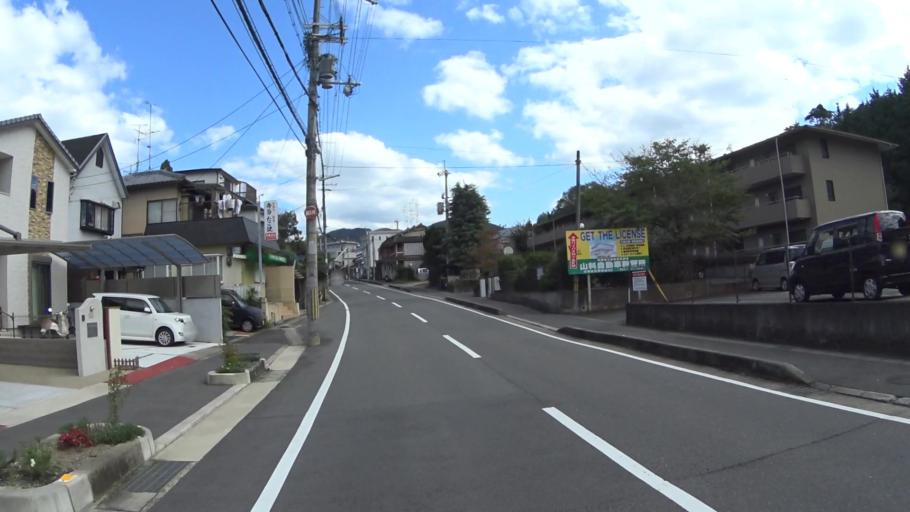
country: JP
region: Kyoto
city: Uji
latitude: 34.9275
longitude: 135.8051
